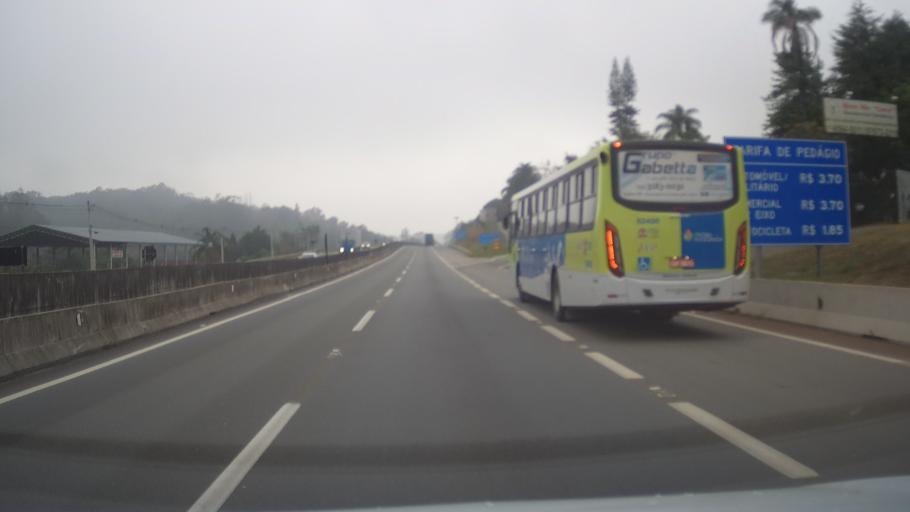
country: BR
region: Sao Paulo
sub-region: Itatiba
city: Itatiba
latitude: -23.0824
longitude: -46.8452
